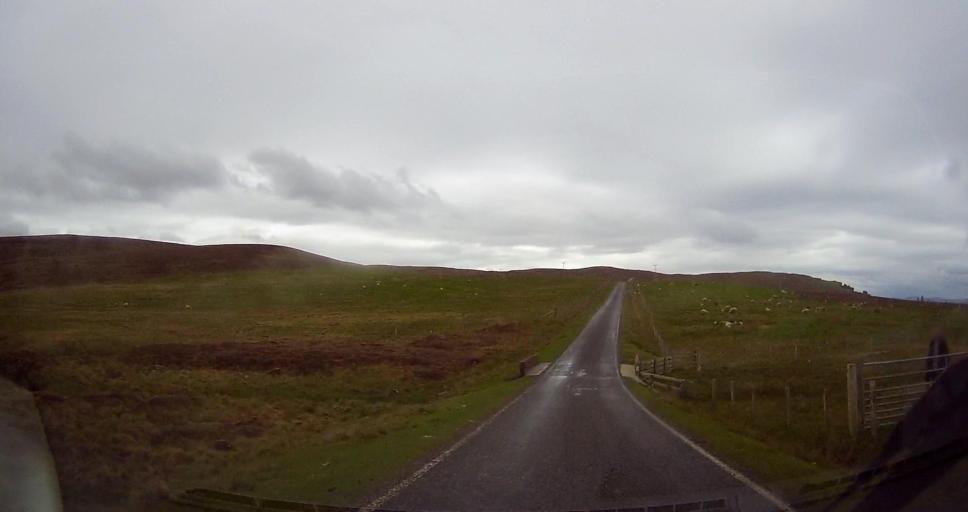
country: GB
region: Scotland
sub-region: Shetland Islands
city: Lerwick
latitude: 60.4944
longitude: -1.5538
